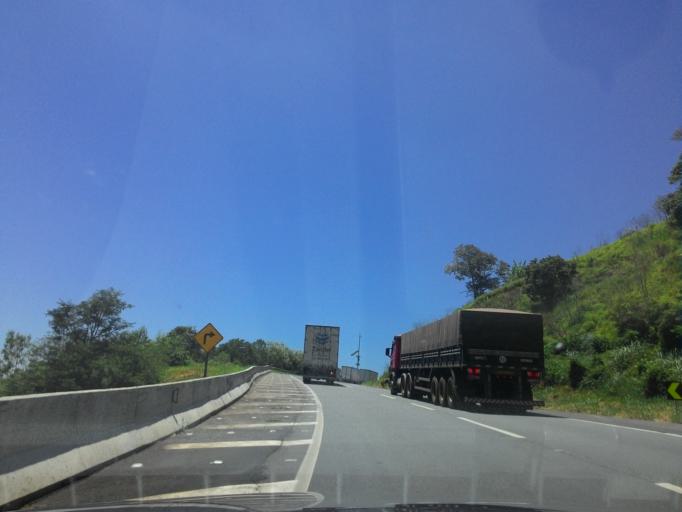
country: BR
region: Sao Paulo
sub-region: Cajati
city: Cajati
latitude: -24.9673
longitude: -48.4772
